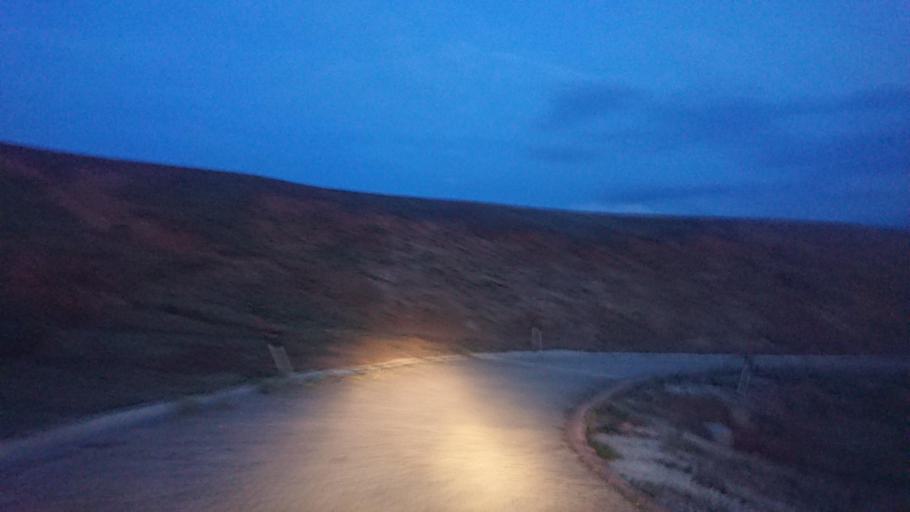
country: TR
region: Aksaray
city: Ortakoy
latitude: 38.6357
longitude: 34.0183
